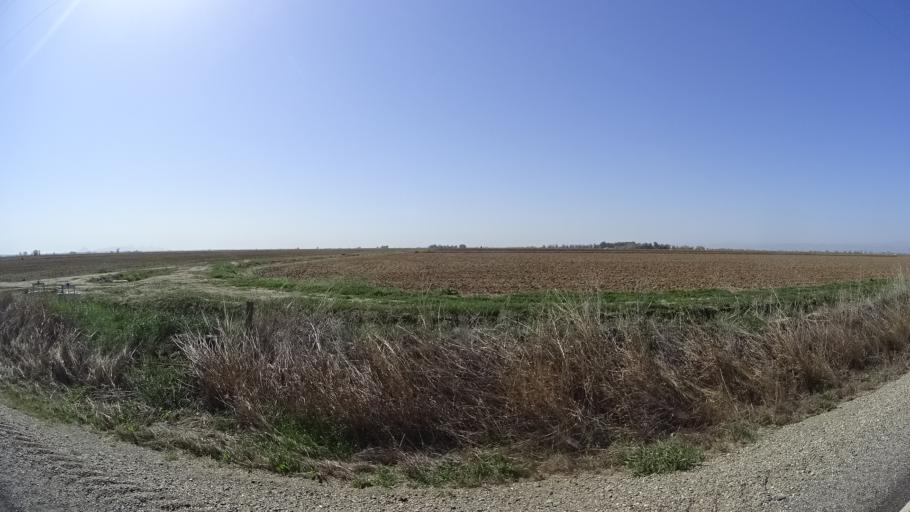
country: US
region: California
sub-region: Glenn County
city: Willows
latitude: 39.4645
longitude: -122.1086
